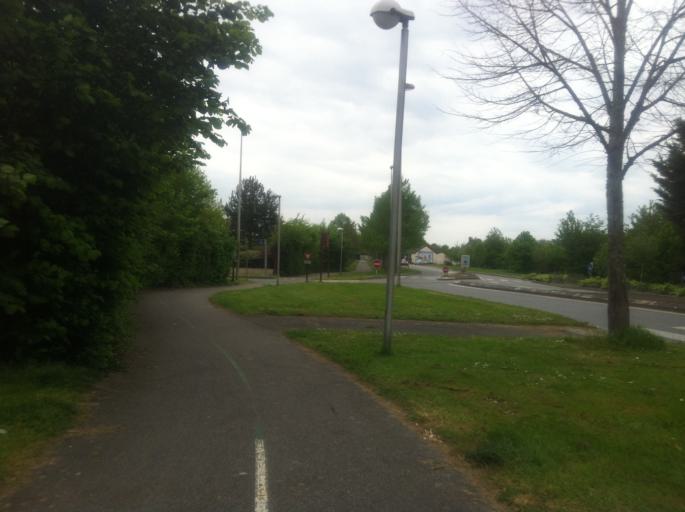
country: FR
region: Brittany
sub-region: Departement d'Ille-et-Vilaine
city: Bruz
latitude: 48.0273
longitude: -1.7301
